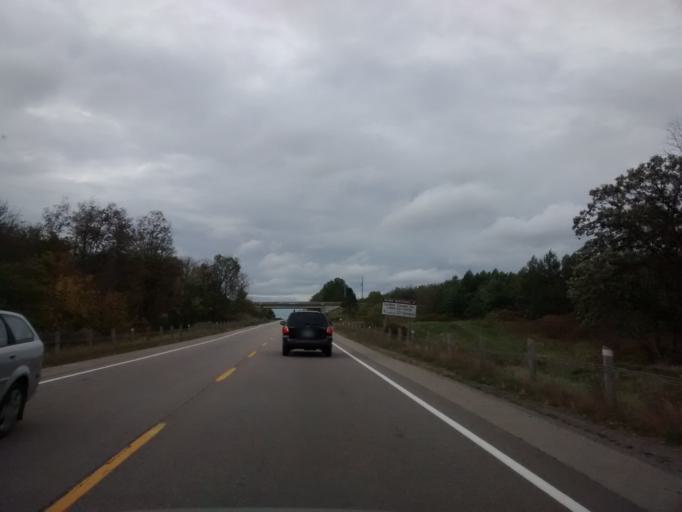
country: CA
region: Ontario
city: Ancaster
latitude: 43.0751
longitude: -79.9733
